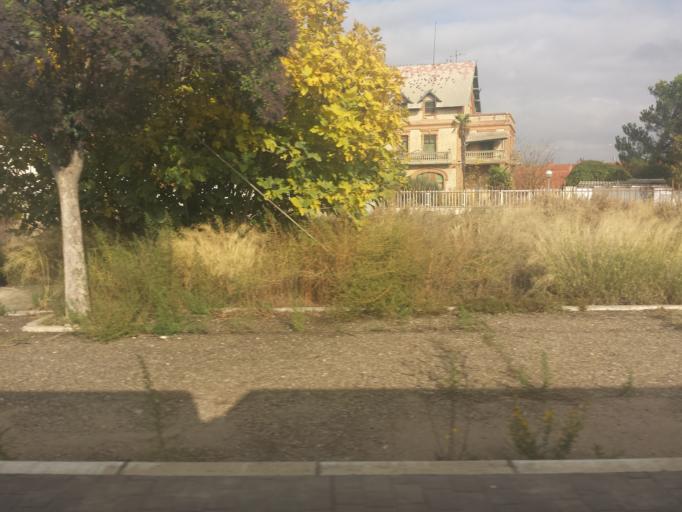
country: ES
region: Aragon
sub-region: Provincia de Zaragoza
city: Luceni
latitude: 41.8265
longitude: -1.2443
